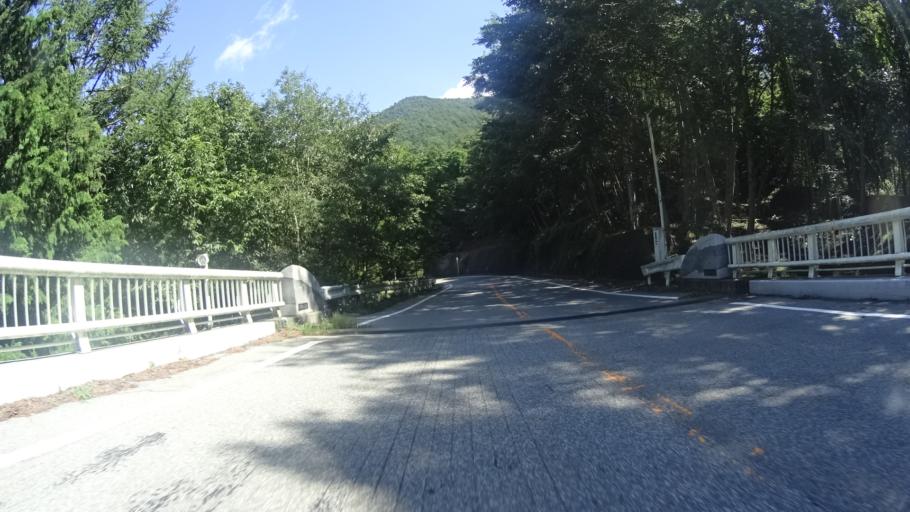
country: JP
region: Yamanashi
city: Enzan
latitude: 35.7506
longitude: 138.8085
